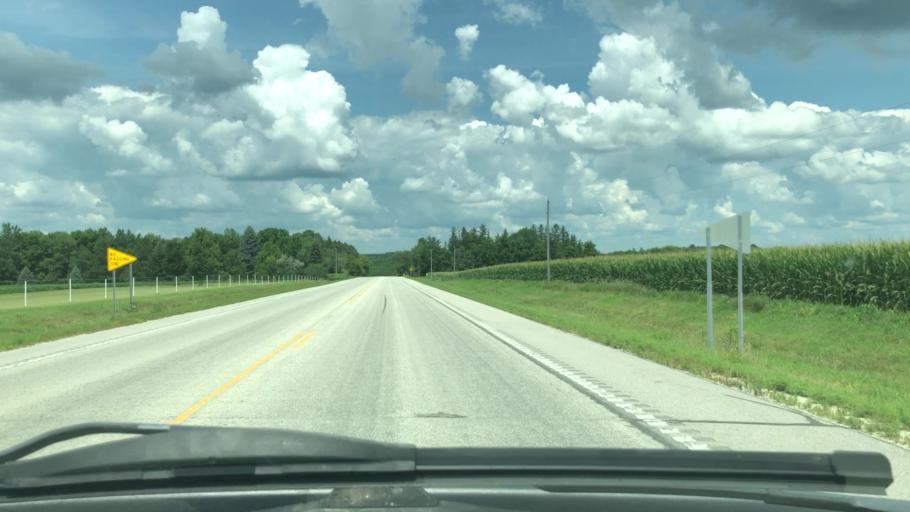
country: US
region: Minnesota
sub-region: Olmsted County
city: Rochester
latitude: 43.9660
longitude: -92.5183
